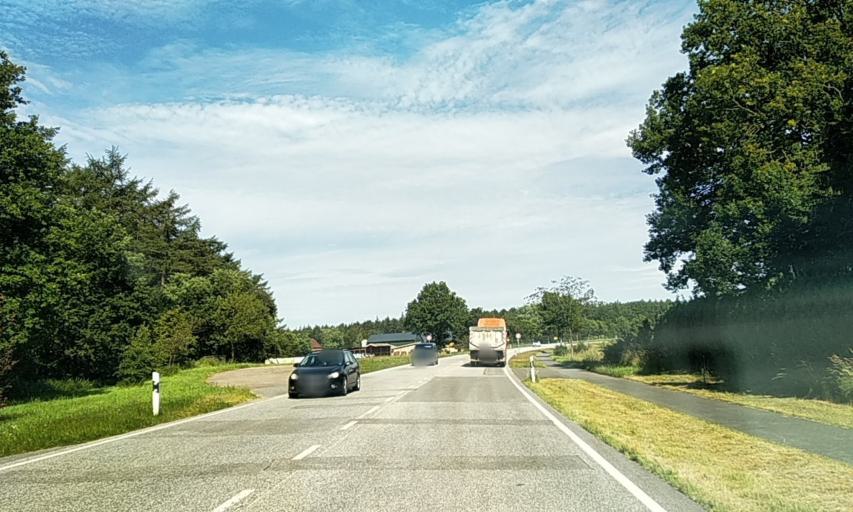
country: DE
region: Schleswig-Holstein
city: Lohe-Fohrden
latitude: 54.3543
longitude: 9.5590
